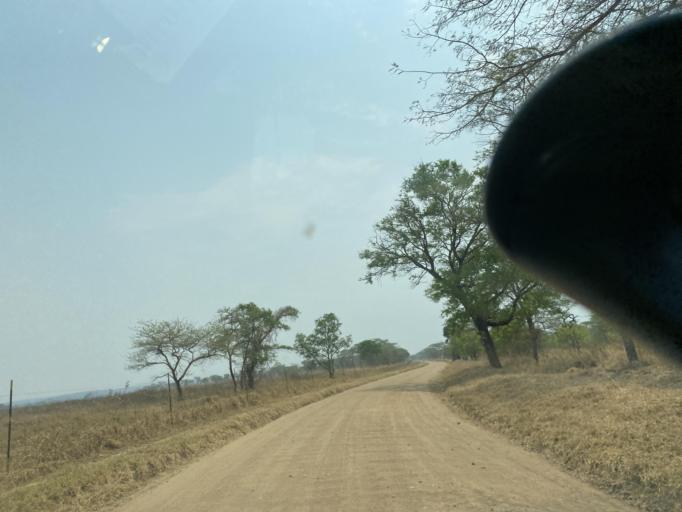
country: ZM
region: Lusaka
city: Kafue
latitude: -15.5941
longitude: 28.1131
